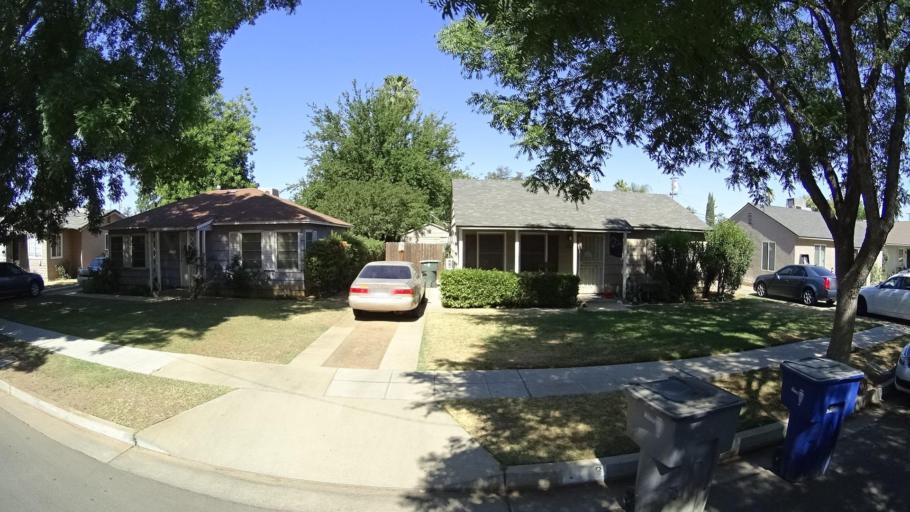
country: US
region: California
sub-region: Fresno County
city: Fresno
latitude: 36.7640
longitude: -119.8199
